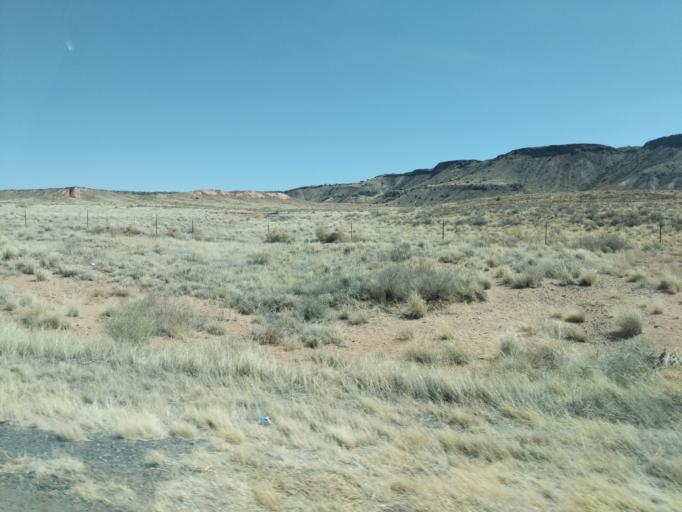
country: US
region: Arizona
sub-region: Navajo County
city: Dilkon
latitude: 35.4430
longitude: -110.0658
